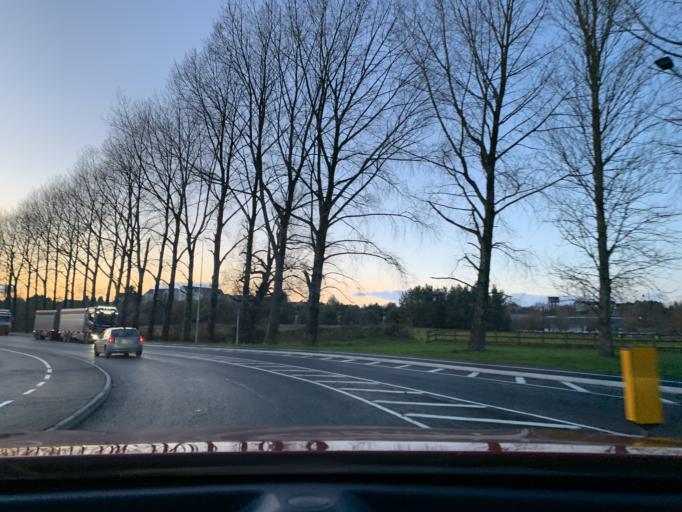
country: IE
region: Connaught
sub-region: County Leitrim
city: Carrick-on-Shannon
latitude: 53.9464
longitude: -8.0799
